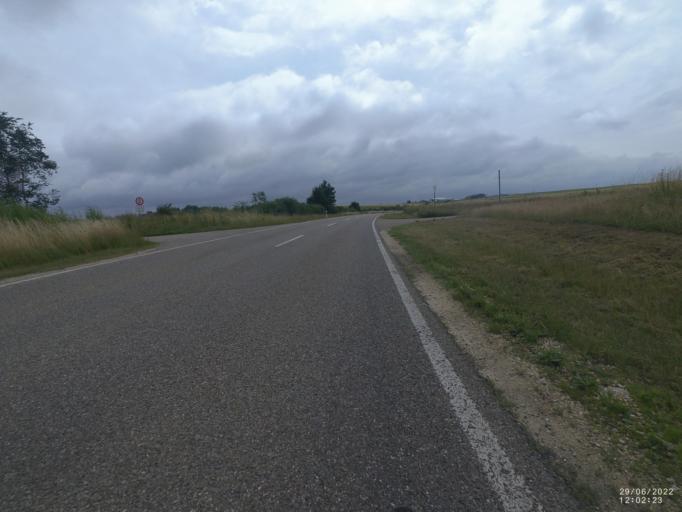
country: DE
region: Baden-Wuerttemberg
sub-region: Regierungsbezirk Stuttgart
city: Gerstetten
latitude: 48.6338
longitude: 9.9948
